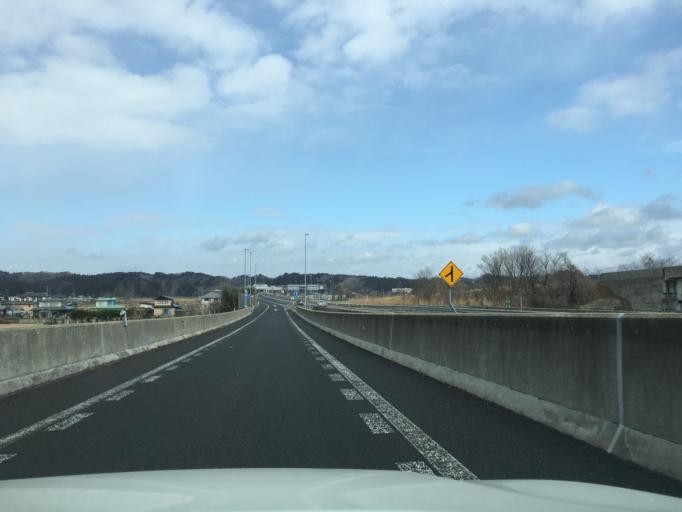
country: JP
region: Akita
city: Akita
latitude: 39.6417
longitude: 140.2103
